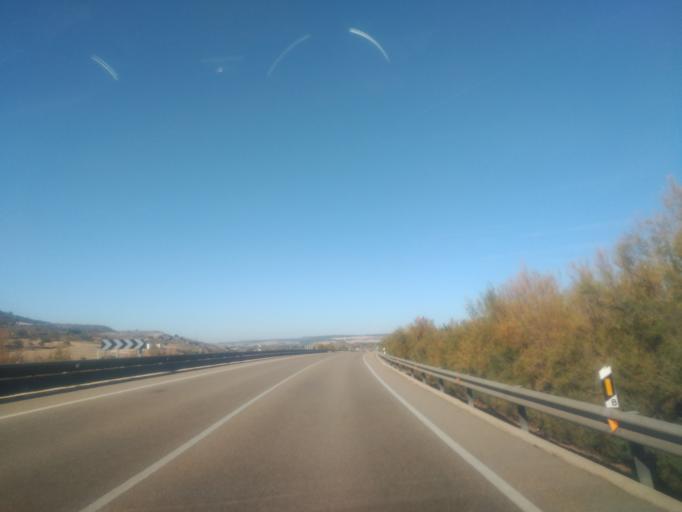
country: ES
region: Castille and Leon
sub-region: Provincia de Valladolid
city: Quintanilla de Arriba
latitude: 41.6179
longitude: -4.2238
